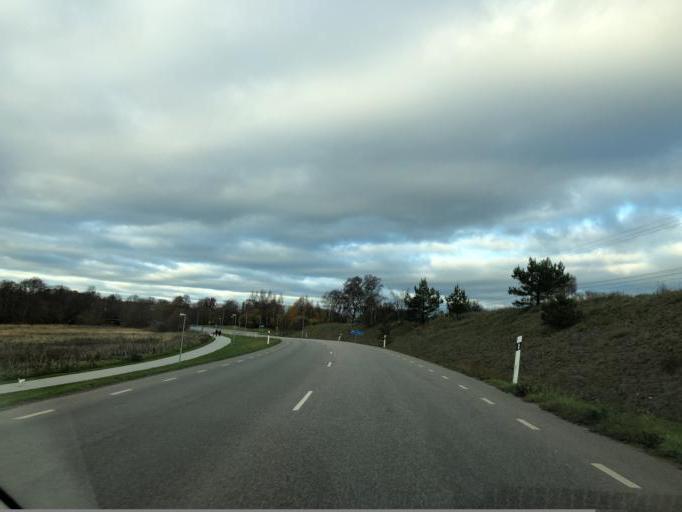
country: SE
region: Skane
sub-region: Kavlinge Kommun
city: Kaevlinge
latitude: 55.7833
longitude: 13.1078
